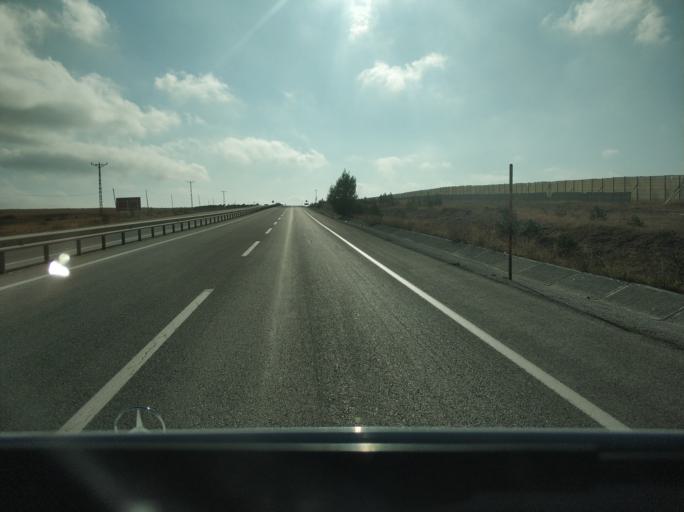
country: TR
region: Sivas
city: Yildizeli
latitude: 39.8351
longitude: 36.4057
